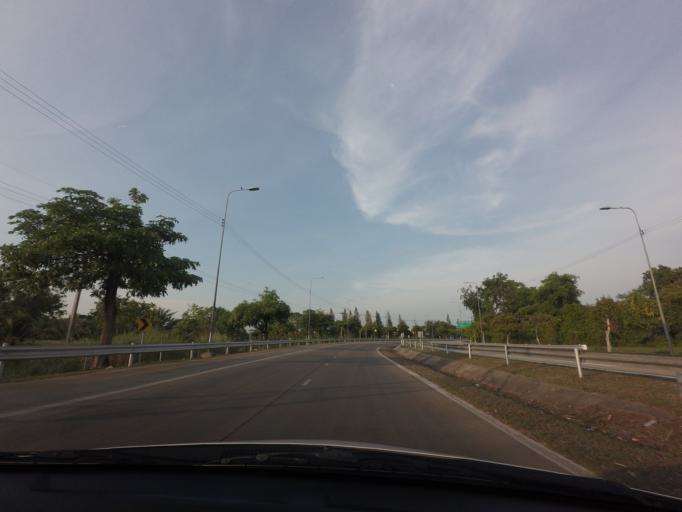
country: TH
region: Phra Nakhon Si Ayutthaya
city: Ban Bang Kadi Pathum Thani
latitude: 14.0045
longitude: 100.5670
